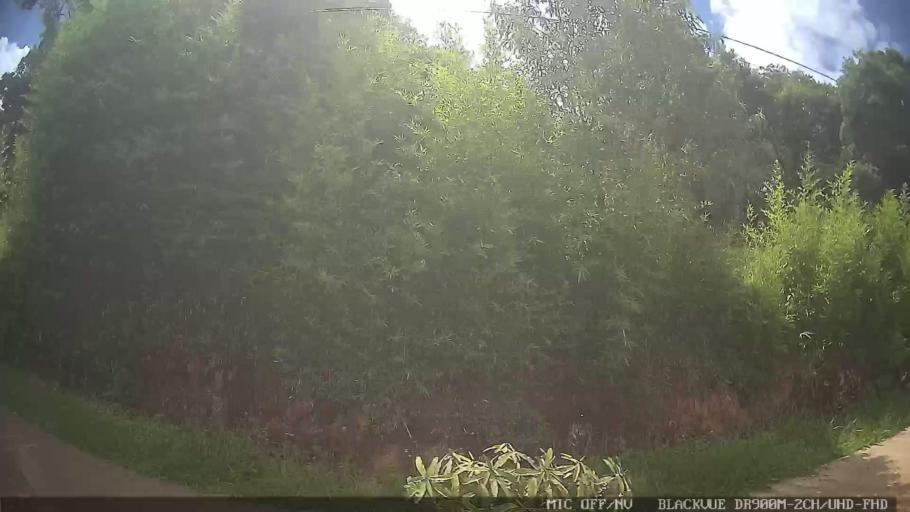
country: BR
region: Minas Gerais
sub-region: Extrema
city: Extrema
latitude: -22.7950
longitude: -46.4464
